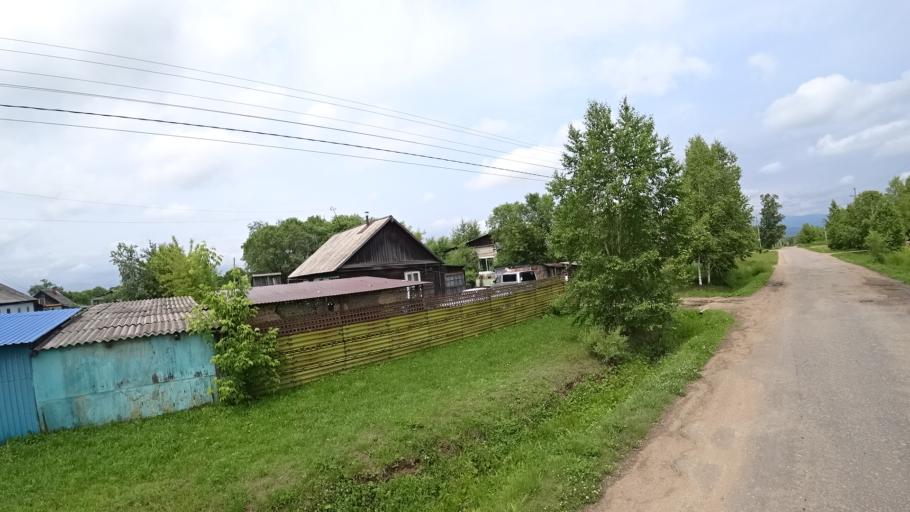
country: RU
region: Primorskiy
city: Novosysoyevka
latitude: 44.2328
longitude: 133.3599
